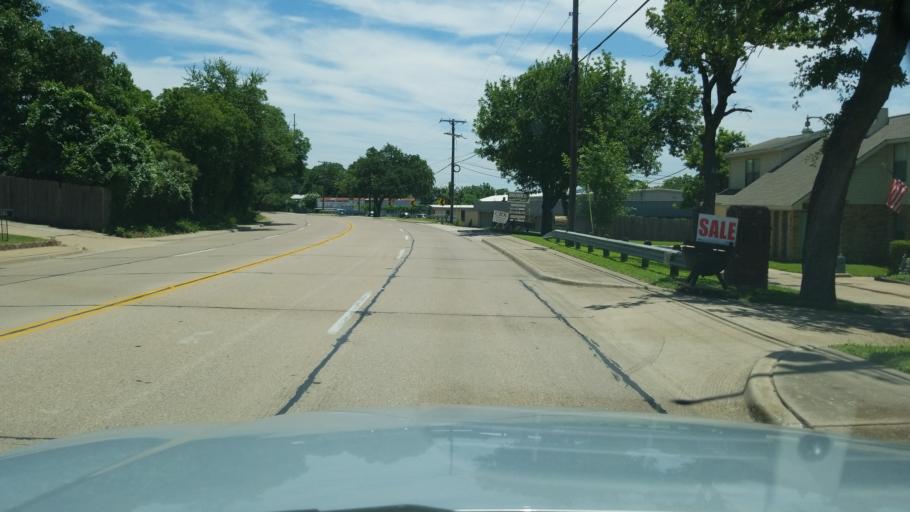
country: US
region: Texas
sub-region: Dallas County
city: Irving
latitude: 32.8012
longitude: -96.9101
